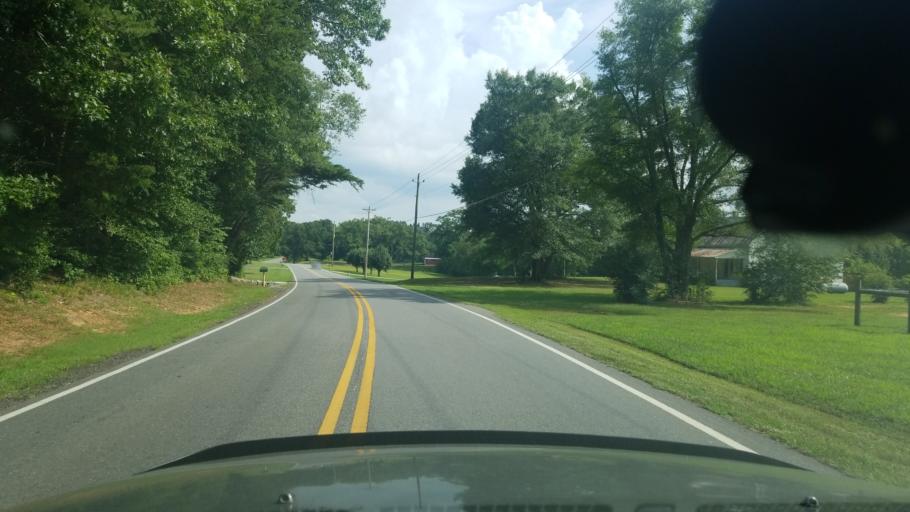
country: US
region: Georgia
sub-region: Hall County
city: Flowery Branch
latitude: 34.2718
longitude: -84.0001
